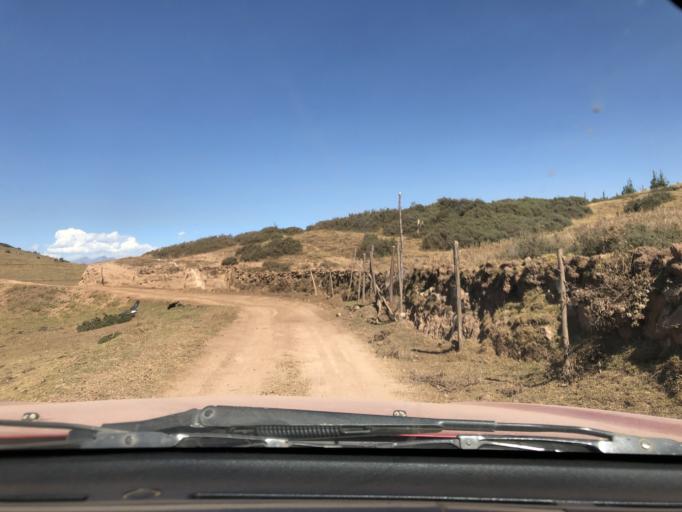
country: PE
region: Ayacucho
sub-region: Provincia de La Mar
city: Pampas
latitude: -13.1877
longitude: -73.8436
